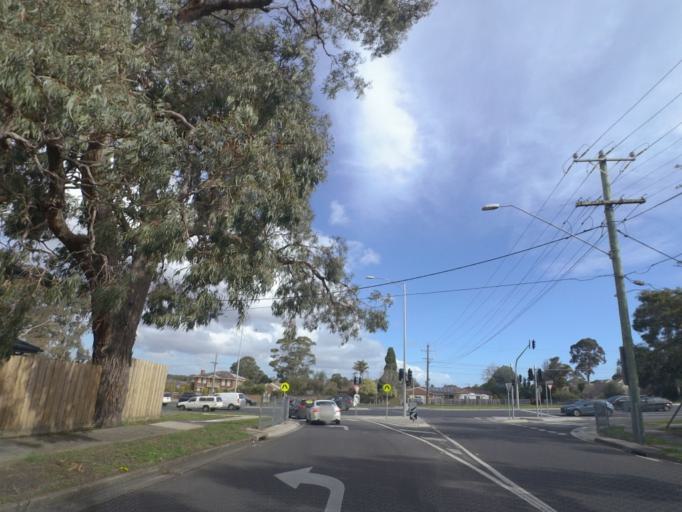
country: AU
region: Victoria
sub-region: Whitehorse
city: Vermont South
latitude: -37.8572
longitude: 145.1903
